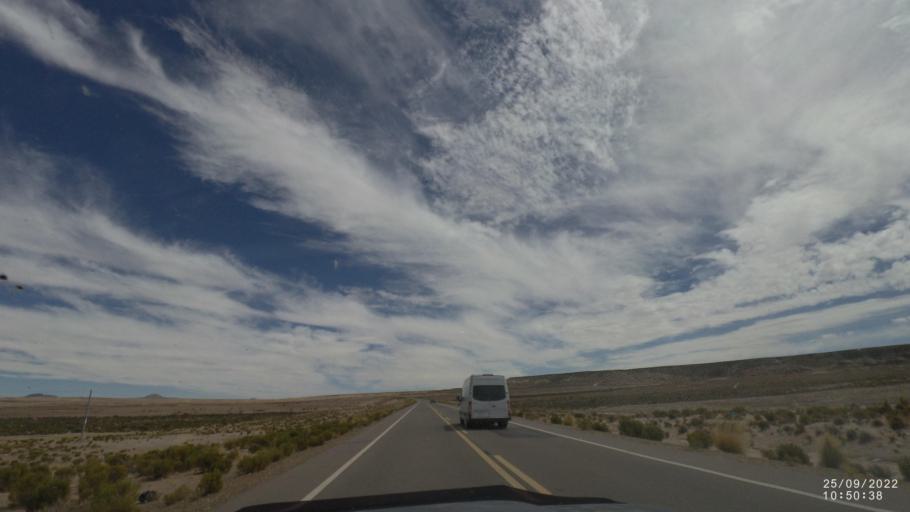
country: BO
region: Oruro
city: Challapata
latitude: -19.5729
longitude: -66.8398
